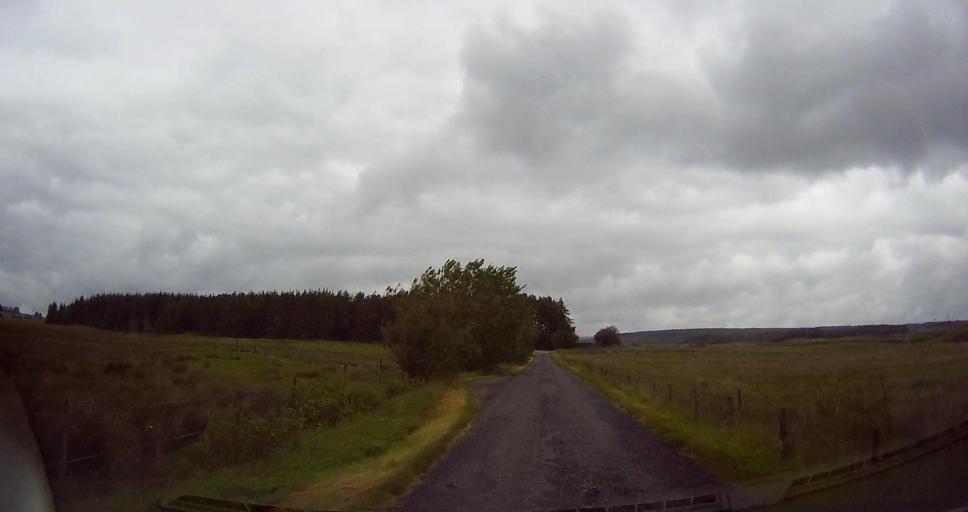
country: GB
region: Scotland
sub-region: Highland
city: Alness
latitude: 58.0653
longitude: -4.4260
